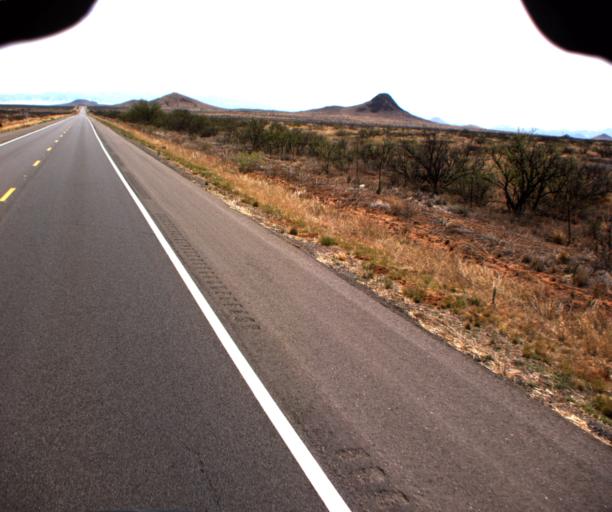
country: US
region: Arizona
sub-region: Cochise County
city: Tombstone
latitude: 31.9054
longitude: -109.7820
